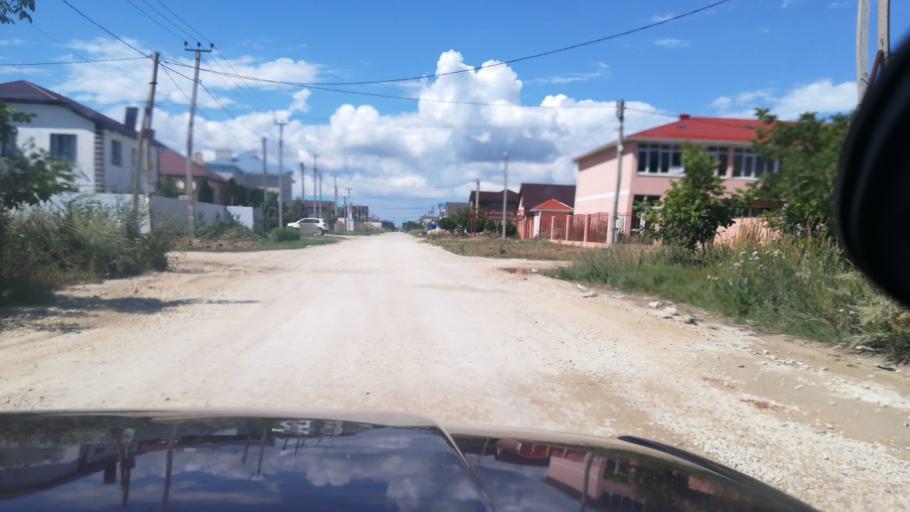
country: RU
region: Krasnodarskiy
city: Vityazevo
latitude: 45.0036
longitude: 37.2969
